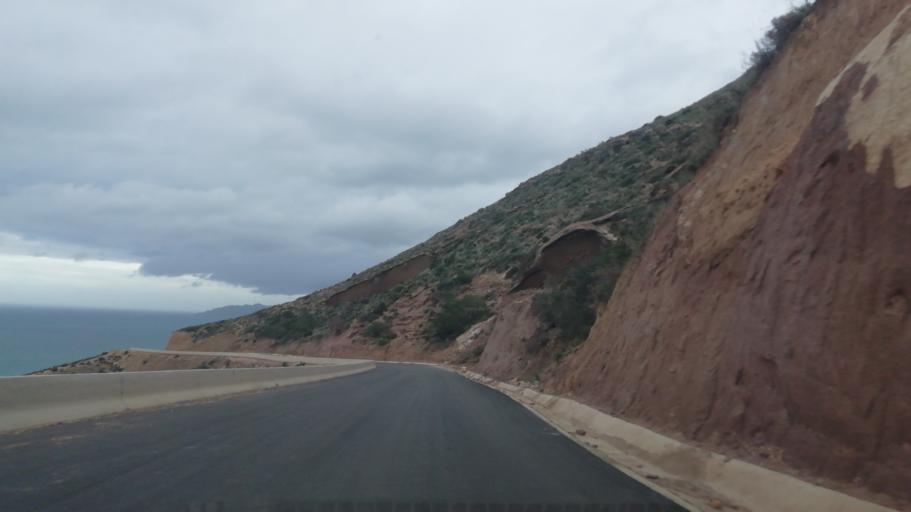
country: DZ
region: Oran
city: Bir el Djir
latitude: 35.7654
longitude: -0.5225
